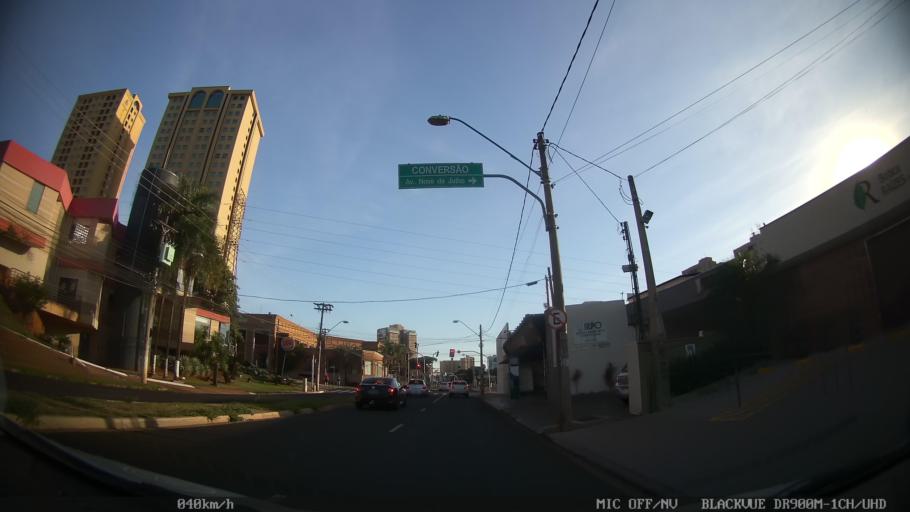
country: BR
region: Sao Paulo
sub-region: Ribeirao Preto
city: Ribeirao Preto
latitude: -21.1942
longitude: -47.8007
